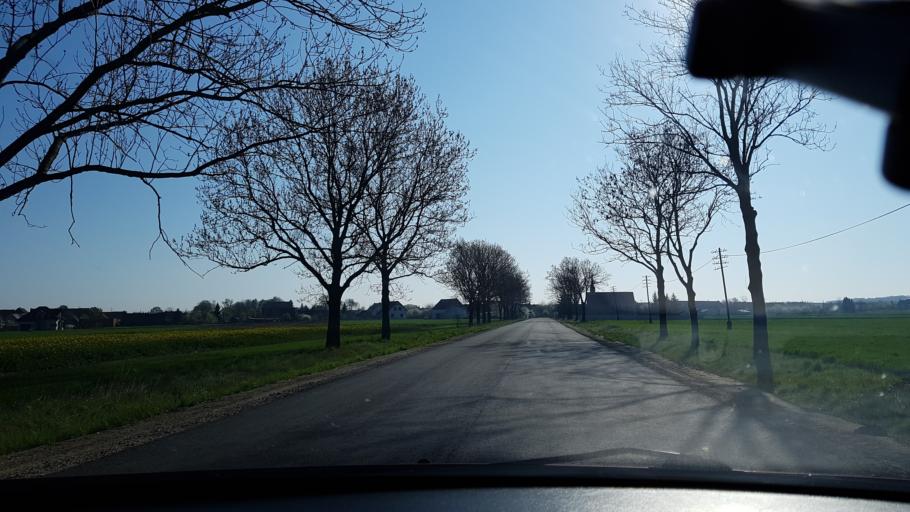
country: CZ
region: Olomoucky
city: Vidnava
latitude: 50.4193
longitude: 17.2187
